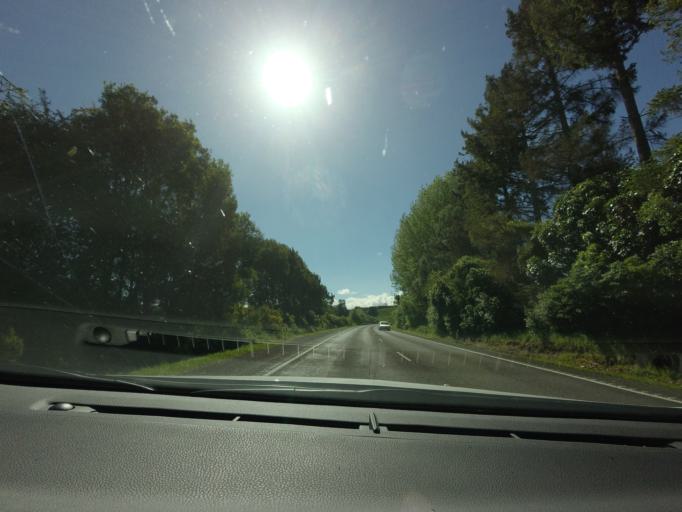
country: NZ
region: Bay of Plenty
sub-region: Rotorua District
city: Rotorua
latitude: -38.0869
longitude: 176.1921
